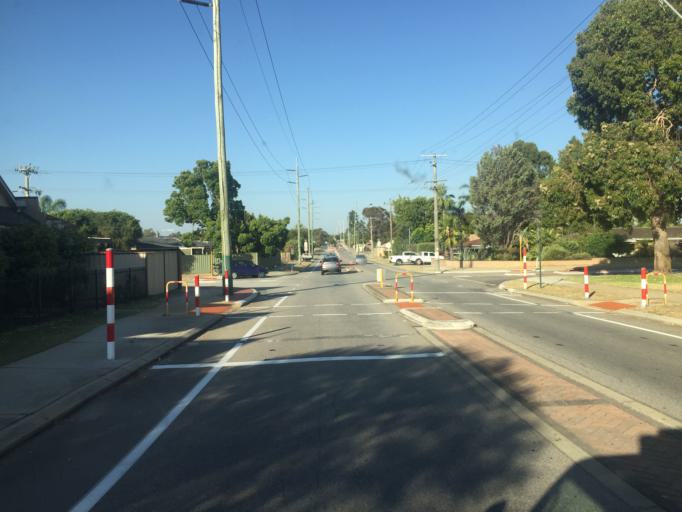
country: AU
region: Western Australia
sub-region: Belmont
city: Belmont
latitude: -31.9568
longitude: 115.9333
